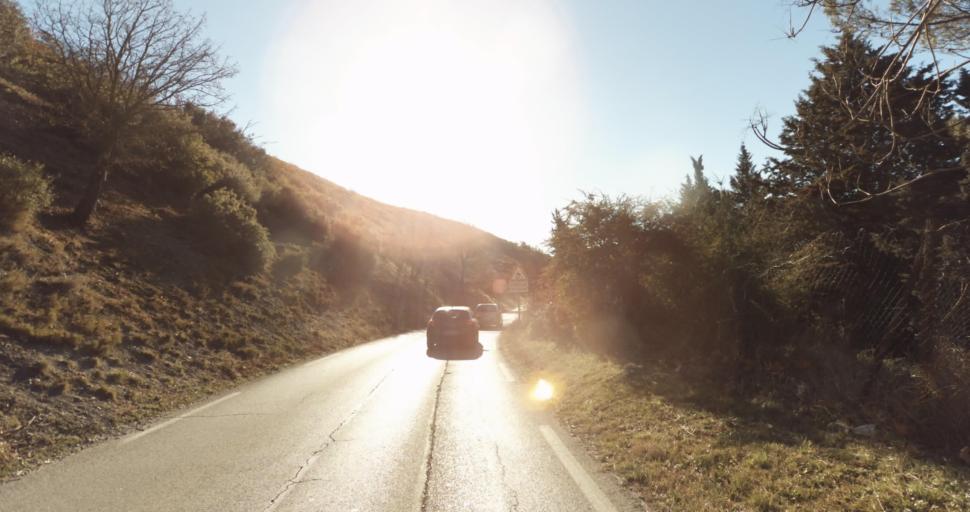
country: FR
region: Provence-Alpes-Cote d'Azur
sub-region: Departement des Bouches-du-Rhone
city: Cadolive
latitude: 43.4066
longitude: 5.5562
